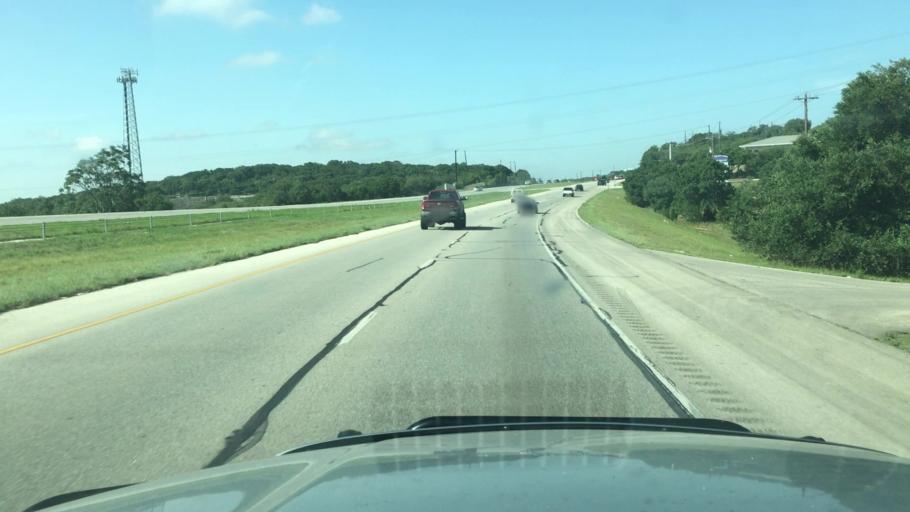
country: US
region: Texas
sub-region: Comal County
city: Bulverde
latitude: 29.7809
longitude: -98.4244
